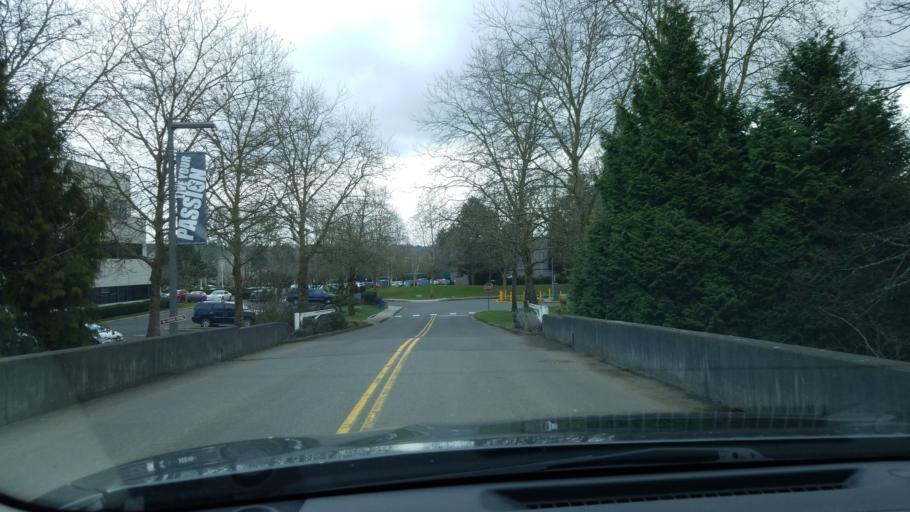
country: US
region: Washington
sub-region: King County
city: Tukwila
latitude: 47.4678
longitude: -122.2488
